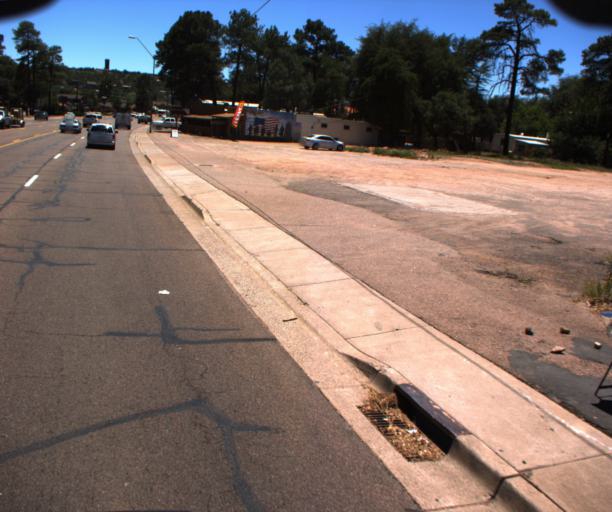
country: US
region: Arizona
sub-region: Gila County
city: Payson
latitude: 34.2338
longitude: -111.3235
